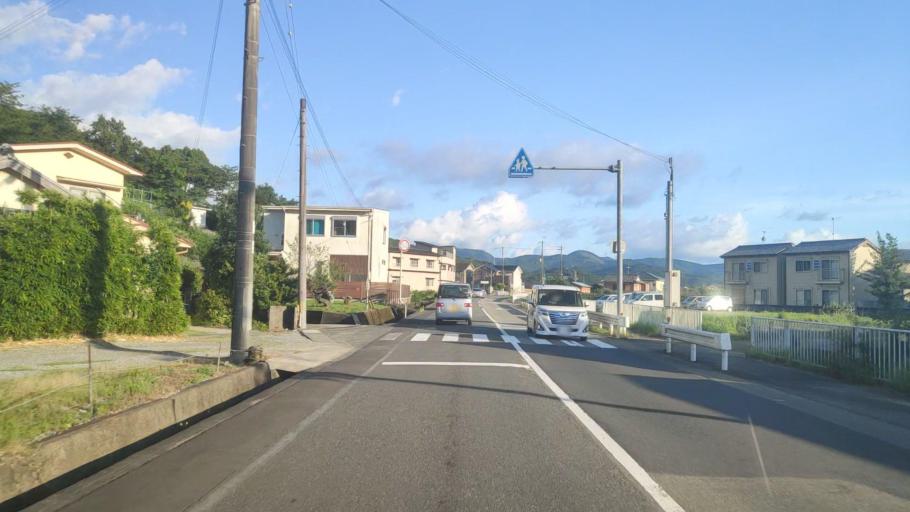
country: JP
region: Wakayama
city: Tanabe
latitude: 33.7223
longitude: 135.4453
